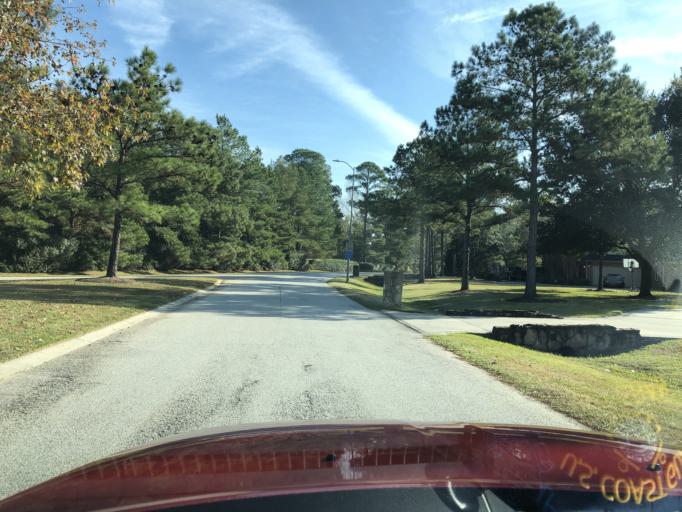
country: US
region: Texas
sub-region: Harris County
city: Tomball
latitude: 30.0400
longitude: -95.5625
